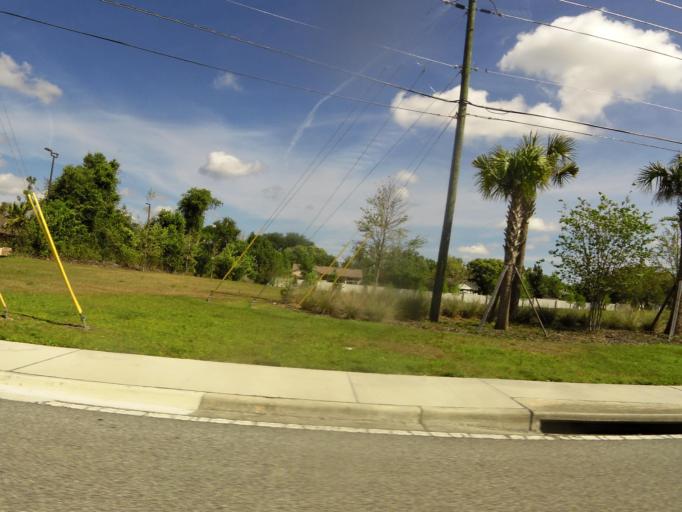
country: US
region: Florida
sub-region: Volusia County
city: Lake Helen
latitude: 28.9478
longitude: -81.2411
